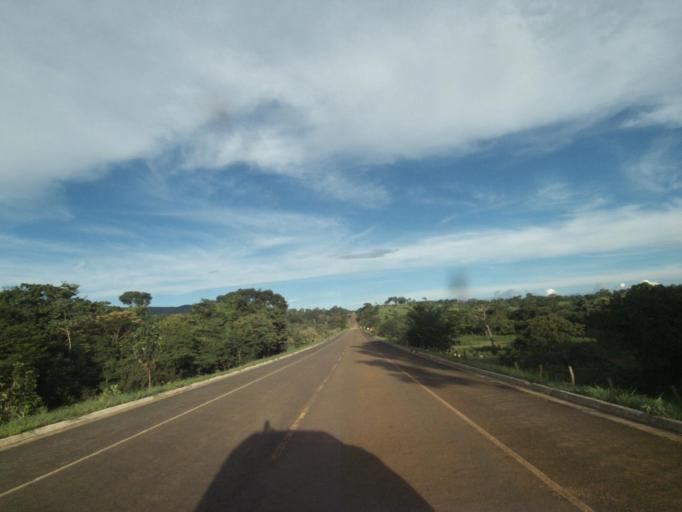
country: BR
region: Goias
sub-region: Jaragua
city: Jaragua
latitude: -15.8422
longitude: -49.3500
